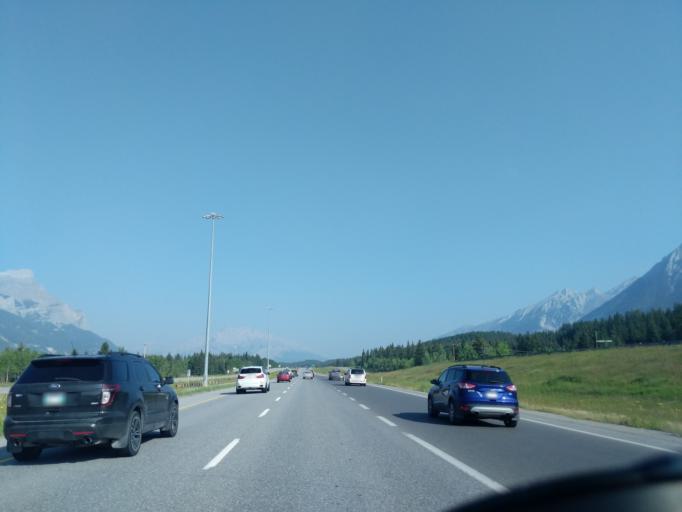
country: CA
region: Alberta
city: Canmore
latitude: 51.1110
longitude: -115.3696
